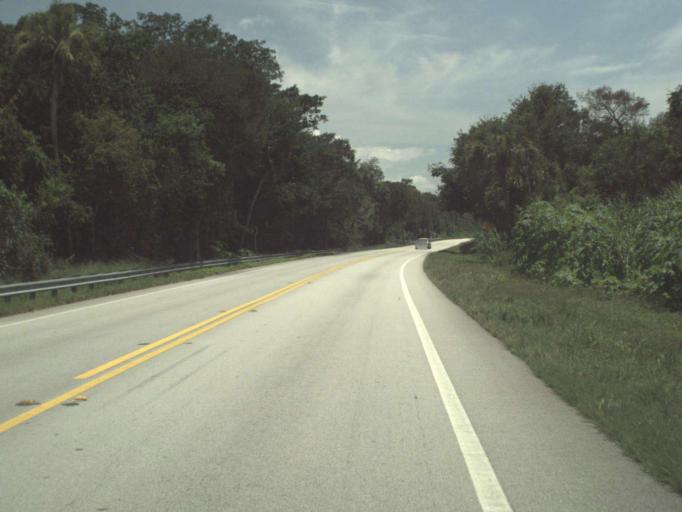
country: US
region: Florida
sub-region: Martin County
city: Indiantown
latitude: 26.9677
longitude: -80.6110
